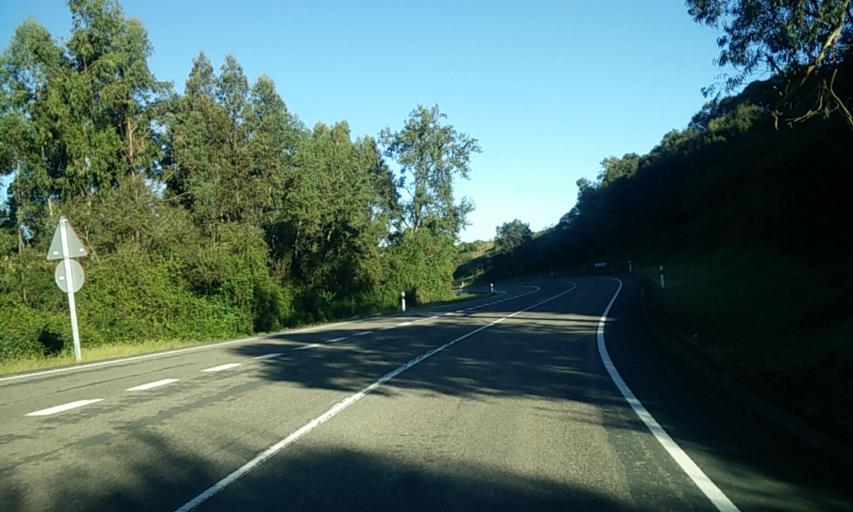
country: ES
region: Cantabria
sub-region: Provincia de Cantabria
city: San Vicente de la Barquera
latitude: 43.3810
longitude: -4.3808
